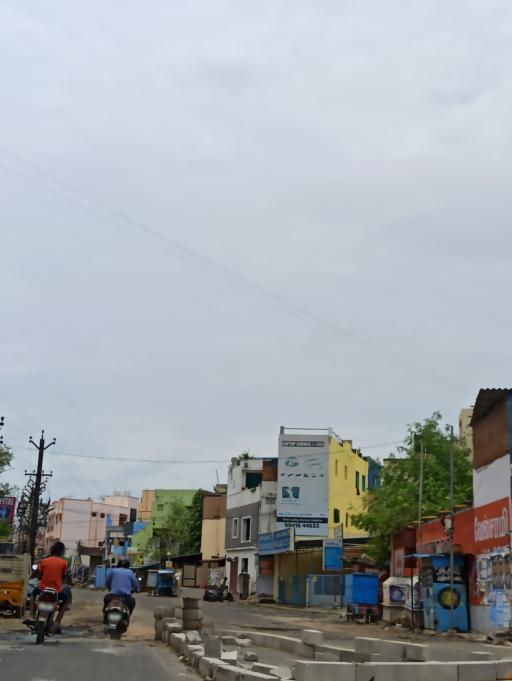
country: IN
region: Tamil Nadu
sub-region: Kancheepuram
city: Vandalur
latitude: 12.9259
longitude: 80.1064
